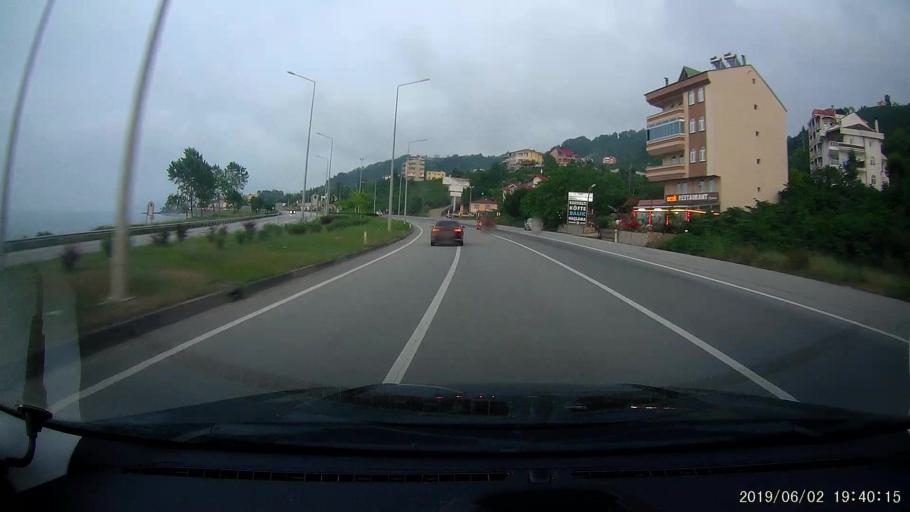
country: TR
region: Giresun
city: Kesap
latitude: 40.9148
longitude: 38.4558
